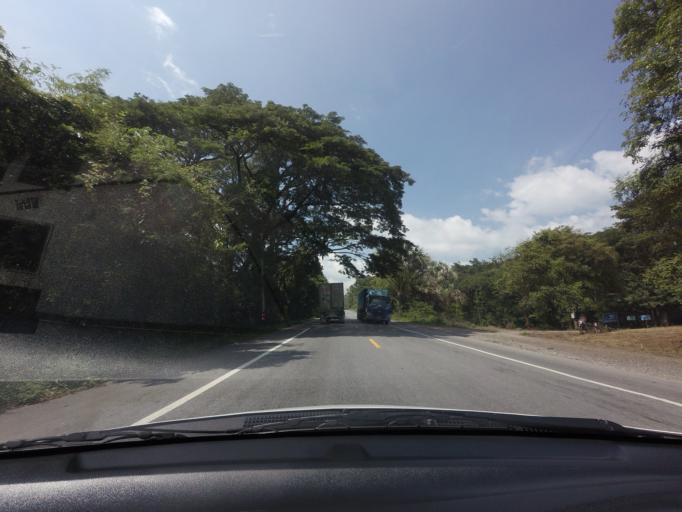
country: TH
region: Nakhon Ratchasima
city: Wang Nam Khiao
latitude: 14.2951
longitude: 101.8812
